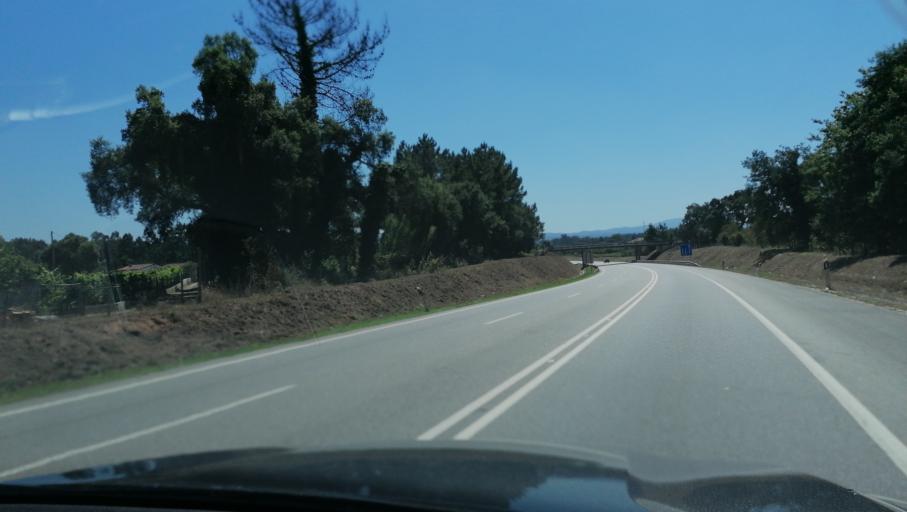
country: PT
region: Aveiro
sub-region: Oliveira do Bairro
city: Oliveira do Bairro
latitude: 40.5438
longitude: -8.4682
